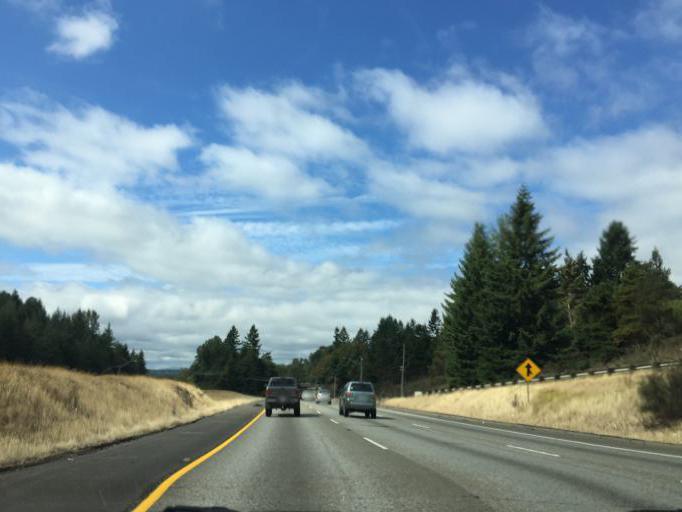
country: US
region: Washington
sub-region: Pierce County
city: DuPont
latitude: 47.0826
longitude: -122.6714
